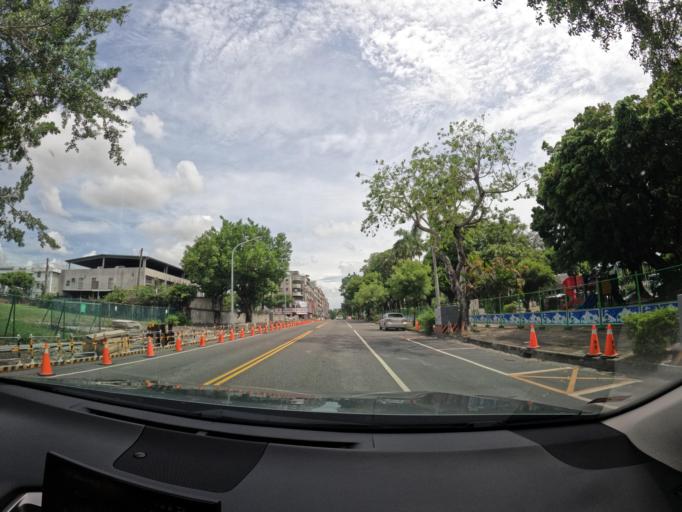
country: TW
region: Kaohsiung
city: Kaohsiung
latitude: 22.6783
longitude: 120.2872
